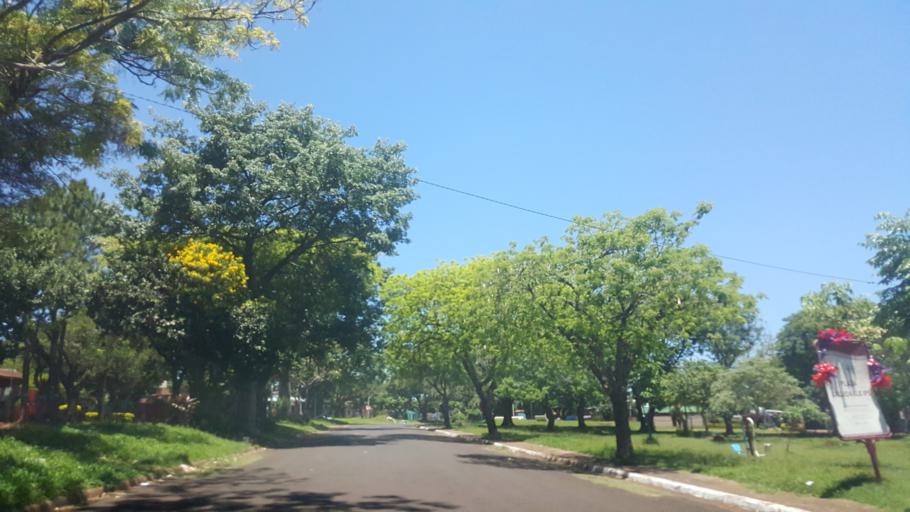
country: AR
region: Misiones
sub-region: Departamento de Capital
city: Posadas
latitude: -27.3880
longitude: -55.9172
